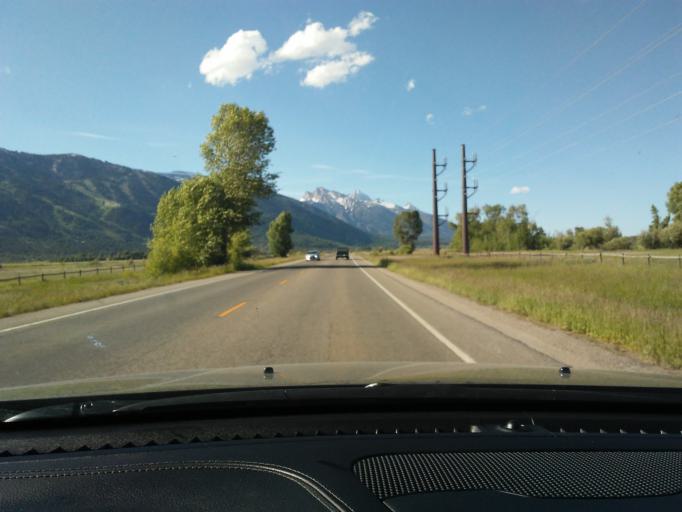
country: US
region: Wyoming
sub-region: Teton County
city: Moose Wilson Road
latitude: 43.5577
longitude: -110.8222
